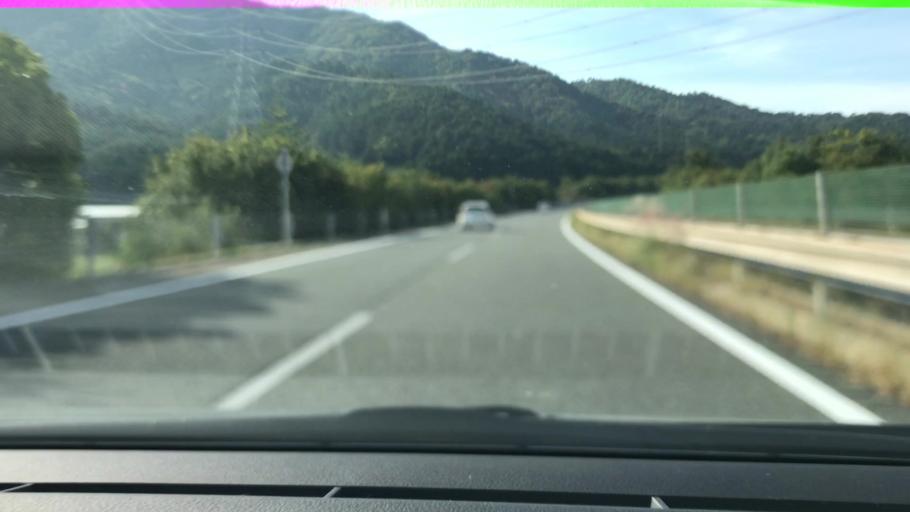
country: JP
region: Hyogo
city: Sasayama
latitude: 35.0374
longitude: 135.1827
